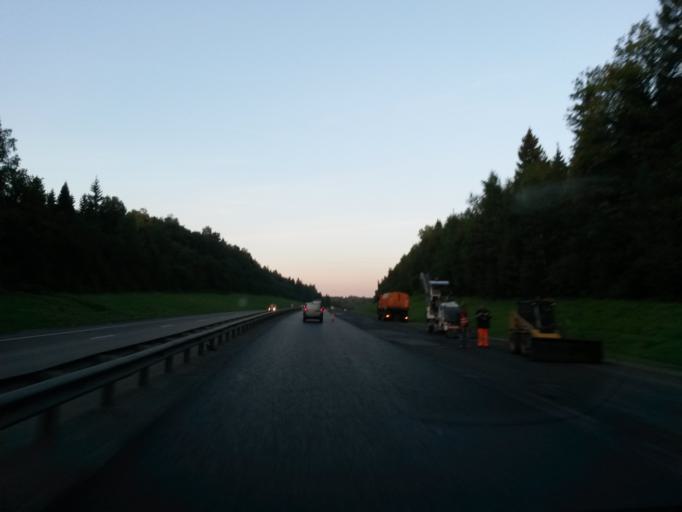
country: RU
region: Moskovskaya
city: Svatkovo
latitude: 56.3050
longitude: 38.2398
